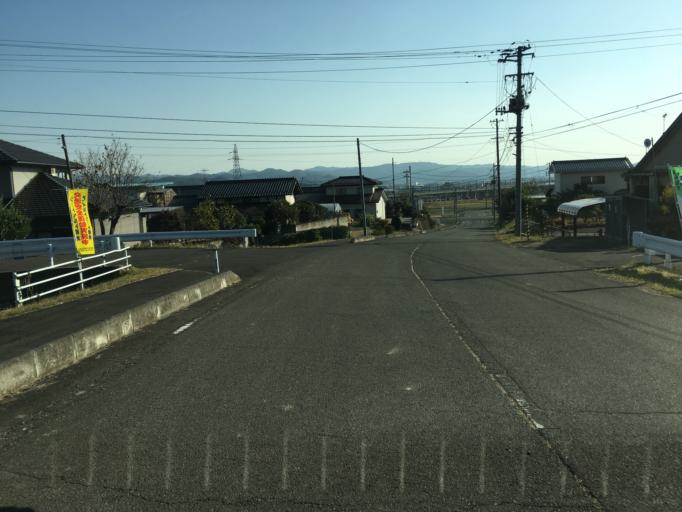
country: JP
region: Fukushima
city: Hobaramachi
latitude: 37.8365
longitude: 140.4973
